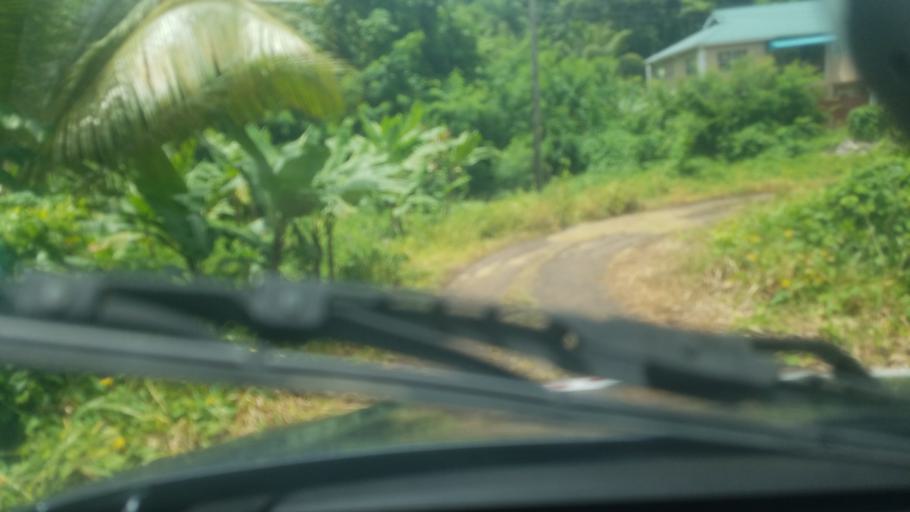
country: LC
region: Gros-Islet
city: Gros Islet
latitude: 14.0513
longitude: -60.9350
